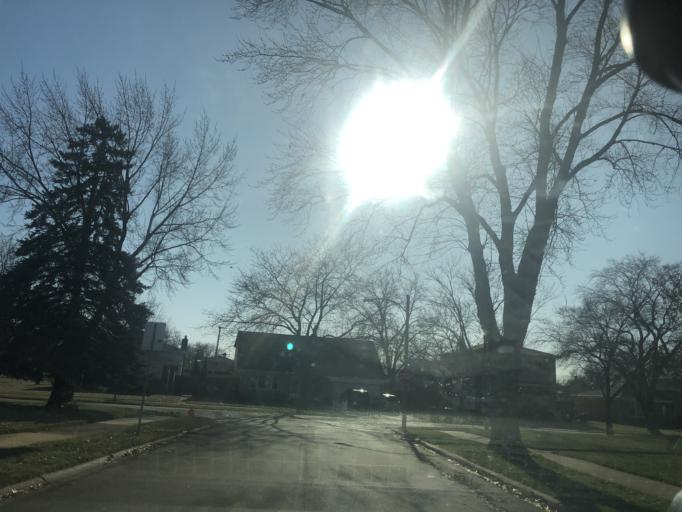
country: US
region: Illinois
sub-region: DuPage County
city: Addison
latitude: 41.9275
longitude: -87.9947
